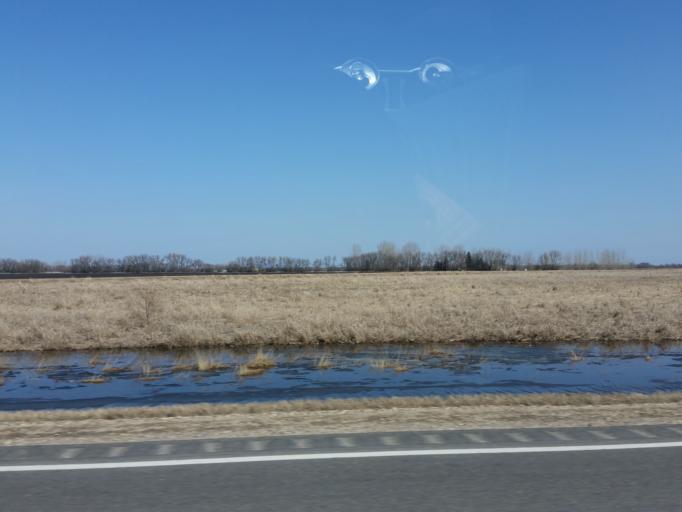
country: US
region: North Dakota
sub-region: Grand Forks County
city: Grand Forks Air Force Base
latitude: 48.1201
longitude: -97.2298
